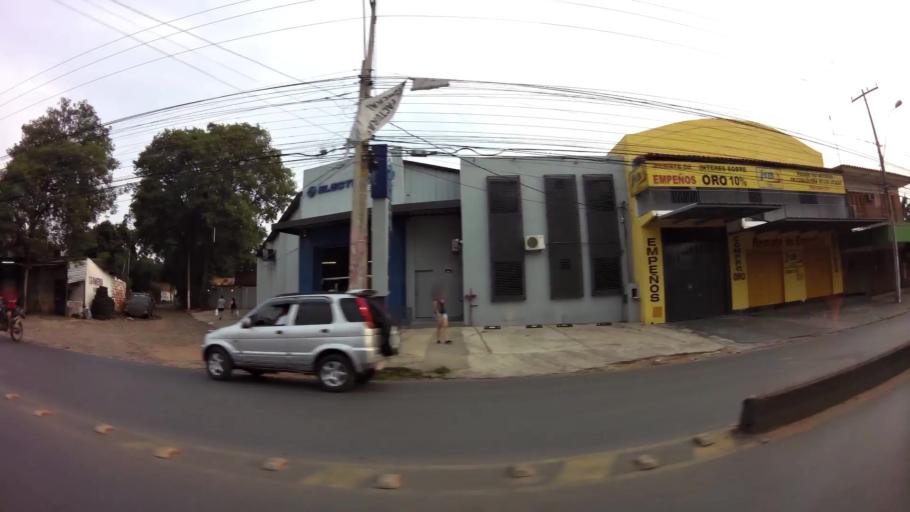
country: PY
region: Central
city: Lambare
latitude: -25.3401
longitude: -57.5949
